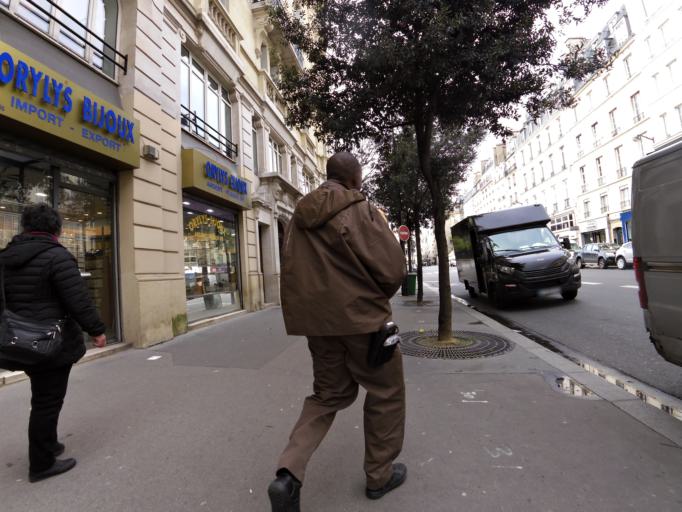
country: FR
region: Ile-de-France
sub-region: Paris
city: Paris
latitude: 48.8659
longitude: 2.3607
